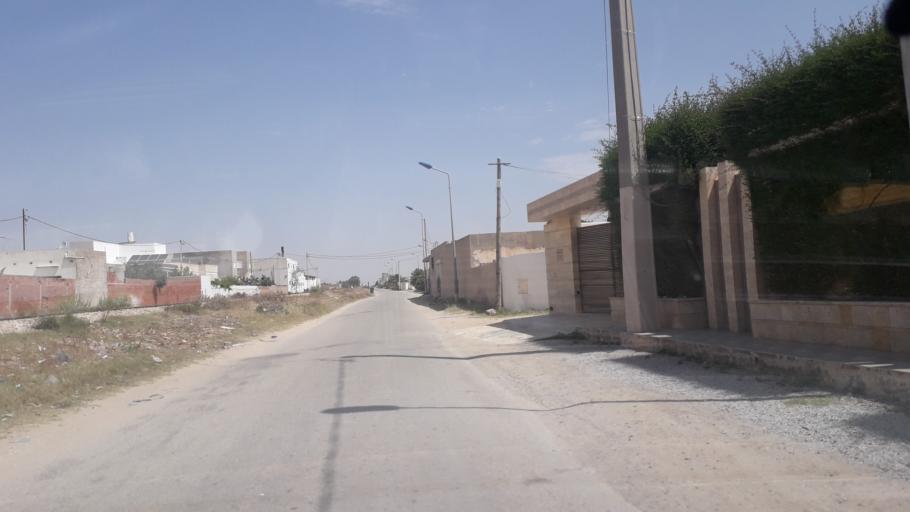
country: TN
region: Safaqis
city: Al Qarmadah
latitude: 34.8264
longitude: 10.7645
